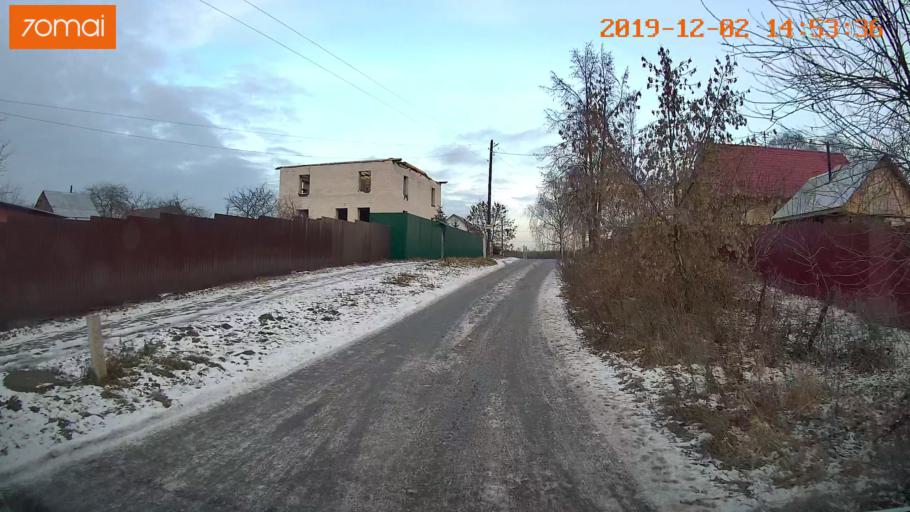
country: RU
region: Ivanovo
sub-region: Gorod Ivanovo
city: Ivanovo
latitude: 56.9758
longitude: 41.0151
